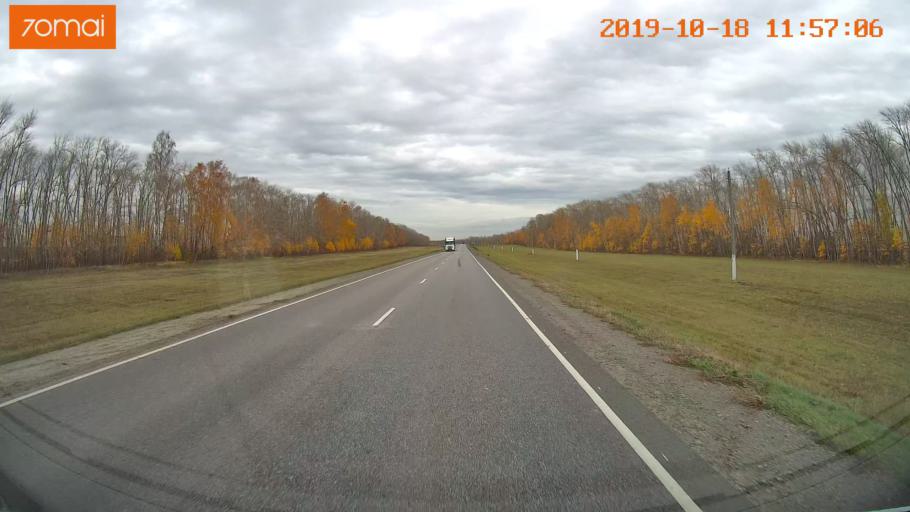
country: RU
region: Rjazan
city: Mikhaylov
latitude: 54.2661
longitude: 39.1341
